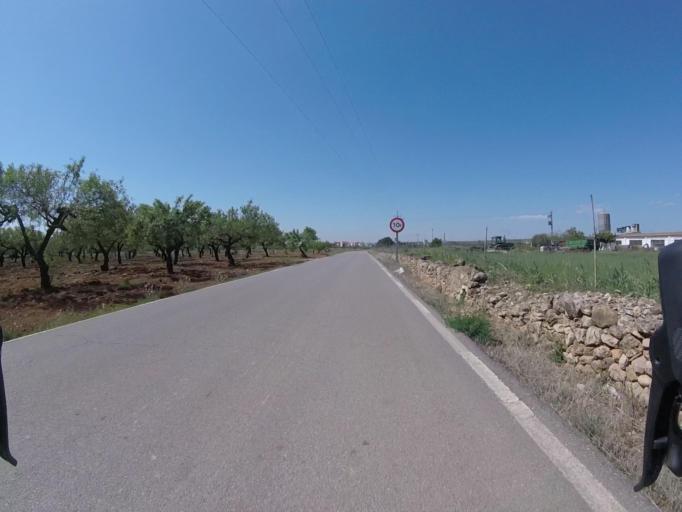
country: ES
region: Valencia
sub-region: Provincia de Castello
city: Benlloch
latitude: 40.2167
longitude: 0.0366
